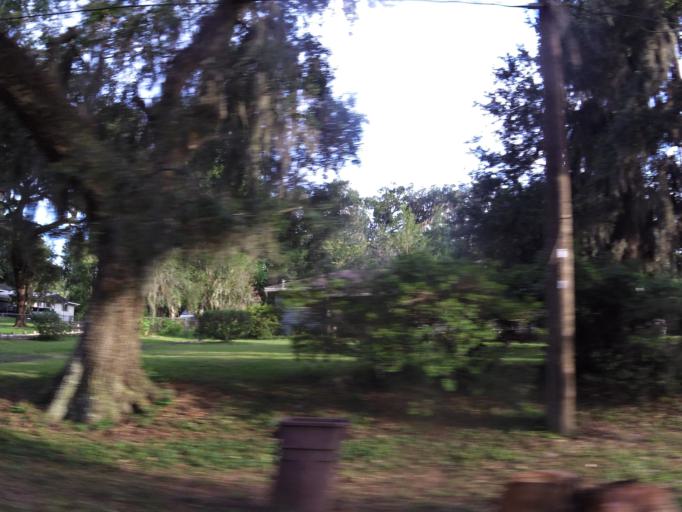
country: US
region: Florida
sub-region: Duval County
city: Jacksonville
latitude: 30.4167
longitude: -81.7150
